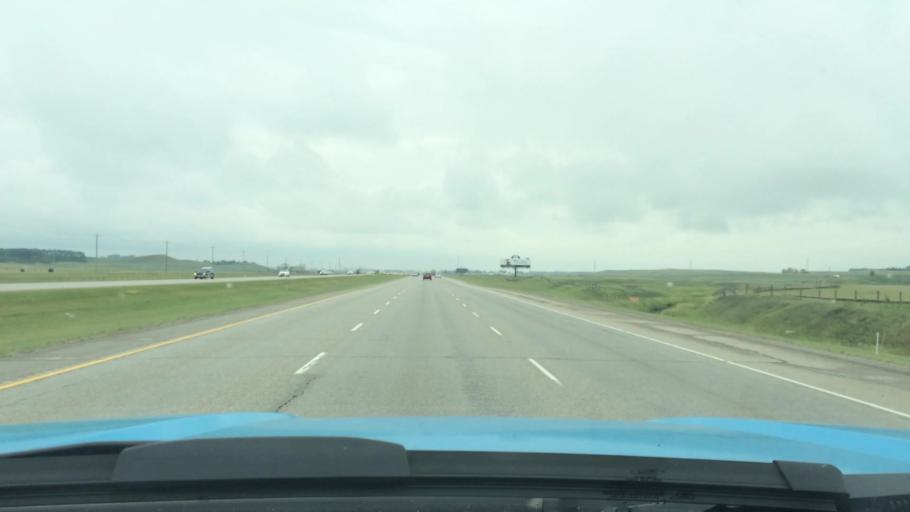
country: CA
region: Alberta
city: Airdrie
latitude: 51.2519
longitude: -114.0017
